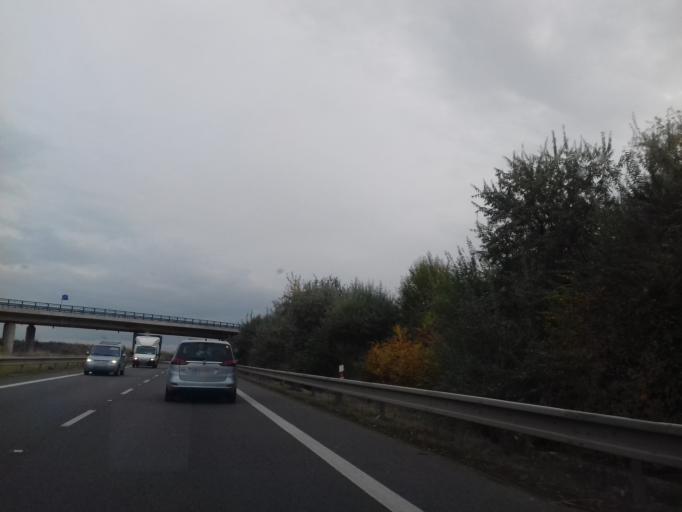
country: CZ
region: Pardubicky
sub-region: Okres Chrudim
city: Chrudim
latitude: 49.9866
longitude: 15.7729
